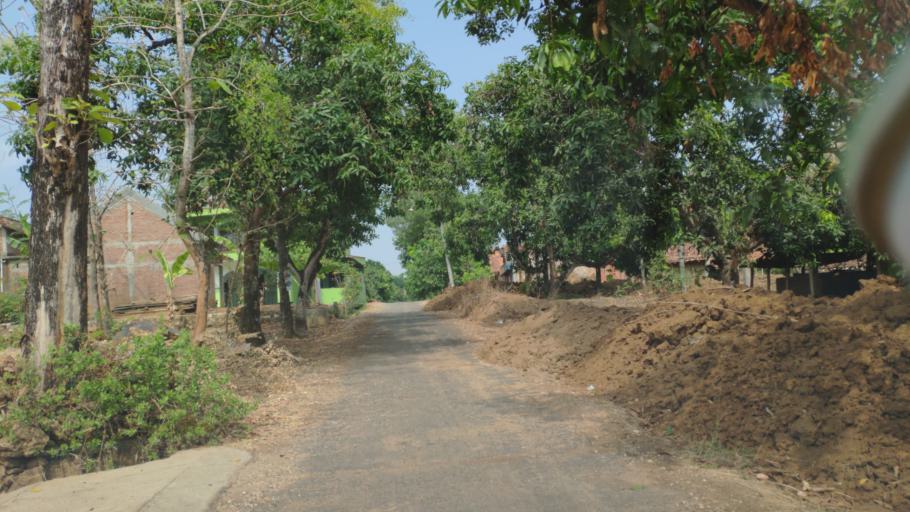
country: ID
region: Central Java
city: Sendangsari
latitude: -6.9769
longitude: 111.3374
